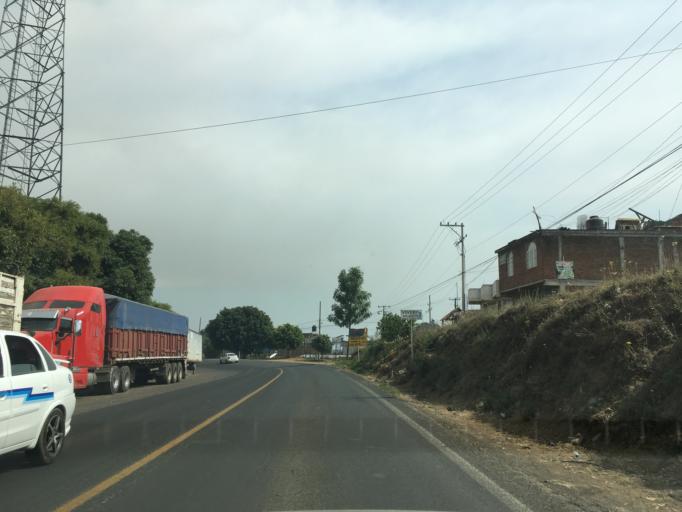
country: MX
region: Michoacan
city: Nuevo San Juan Parangaricutiro
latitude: 19.4079
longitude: -102.1149
